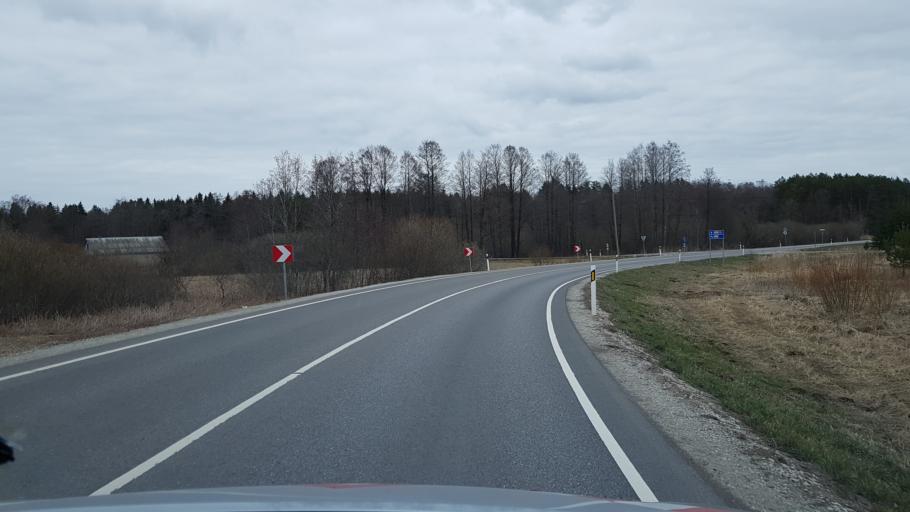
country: EE
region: Ida-Virumaa
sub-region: Narva-Joesuu linn
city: Narva-Joesuu
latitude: 59.4112
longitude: 28.0690
